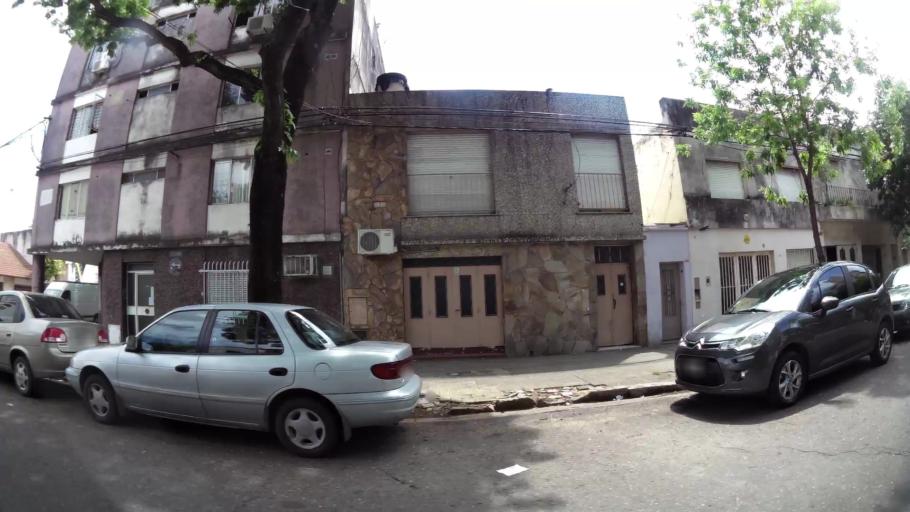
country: AR
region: Santa Fe
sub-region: Departamento de Rosario
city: Rosario
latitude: -32.9602
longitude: -60.6311
